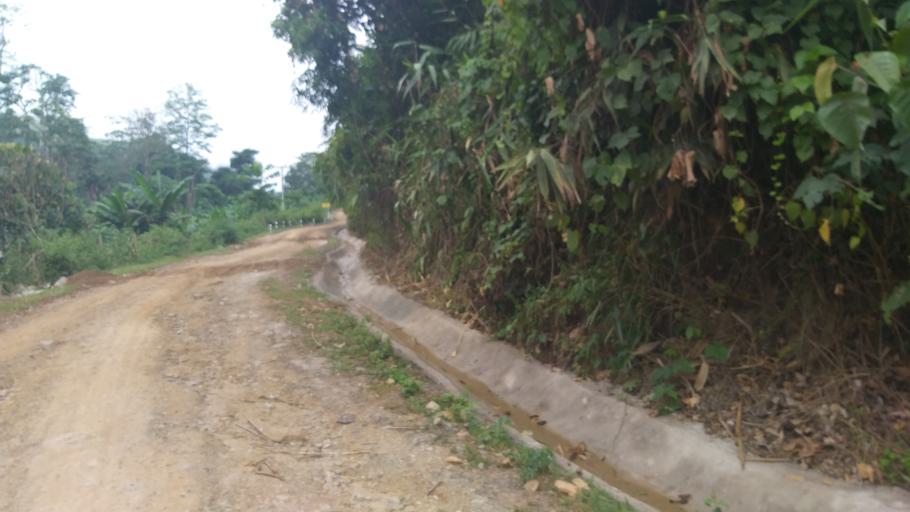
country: LA
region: Phongsali
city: Khoa
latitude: 21.2379
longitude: 102.6708
